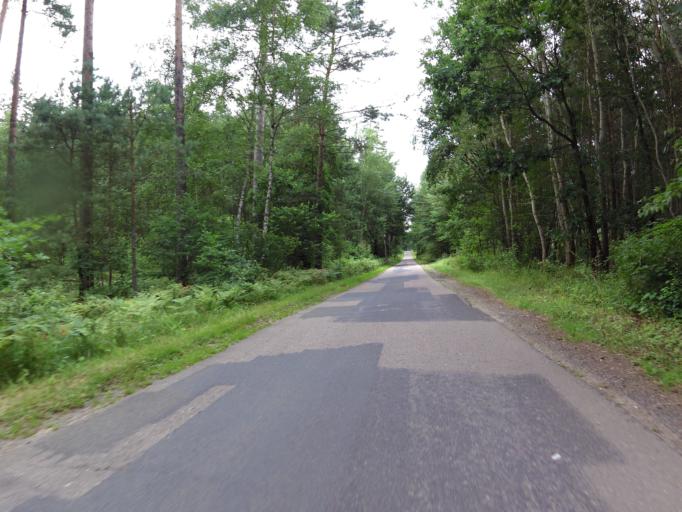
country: DE
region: Brandenburg
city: Furstenberg
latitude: 53.2003
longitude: 13.1721
